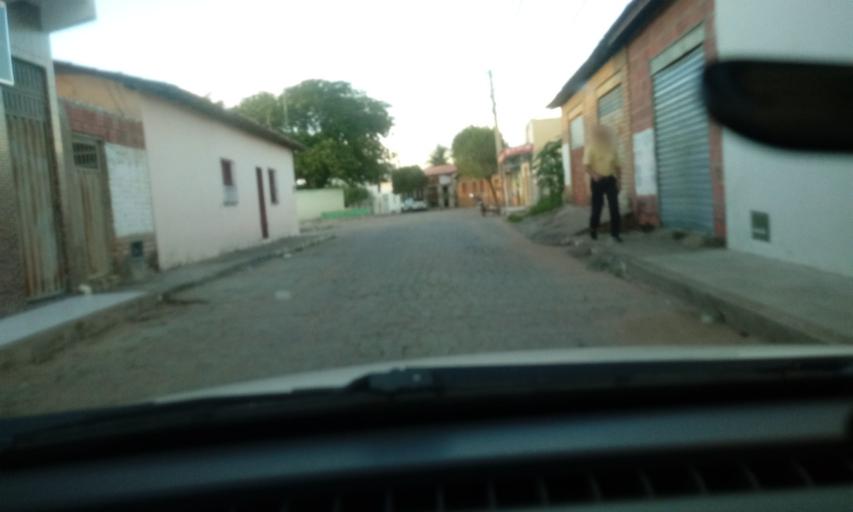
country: BR
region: Bahia
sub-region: Riacho De Santana
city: Riacho de Santana
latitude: -13.9109
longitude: -42.8477
